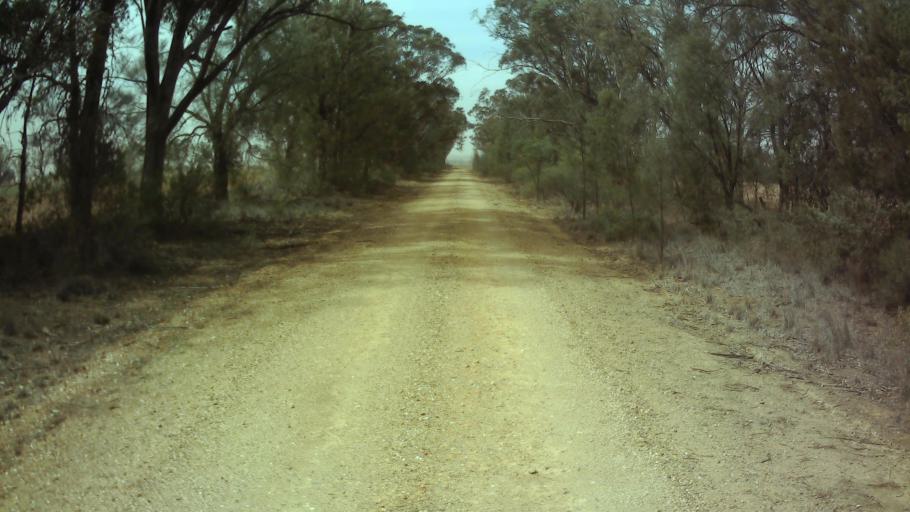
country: AU
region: New South Wales
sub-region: Weddin
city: Grenfell
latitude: -33.7154
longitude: 147.9696
